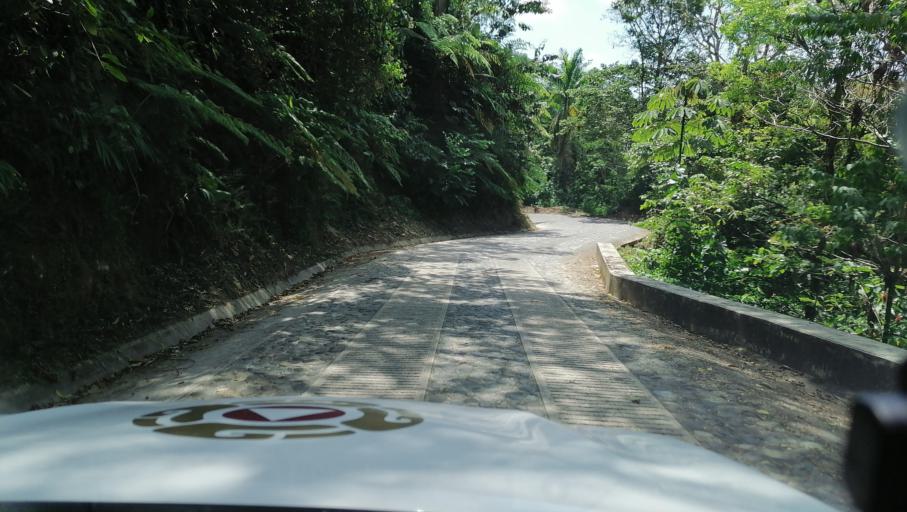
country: MX
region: Chiapas
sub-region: Tapachula
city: Canton Villaflor
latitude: 15.1337
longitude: -92.2914
